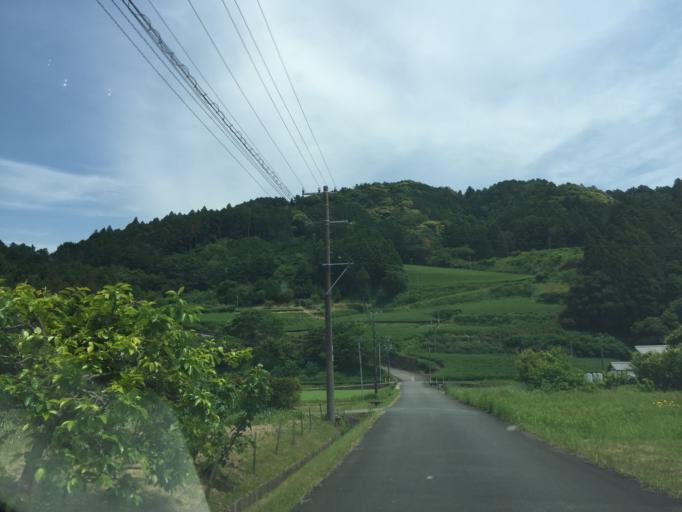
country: JP
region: Shizuoka
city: Mori
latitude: 34.8288
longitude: 137.9654
